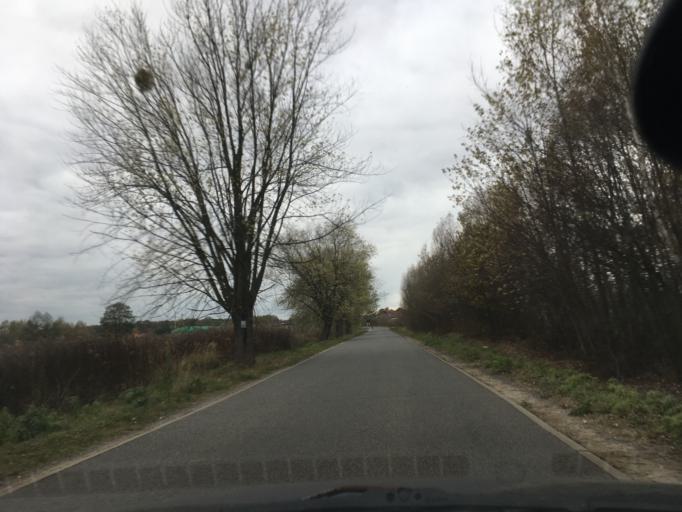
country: PL
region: Lodz Voivodeship
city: Zabia Wola
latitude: 52.0274
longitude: 20.7021
